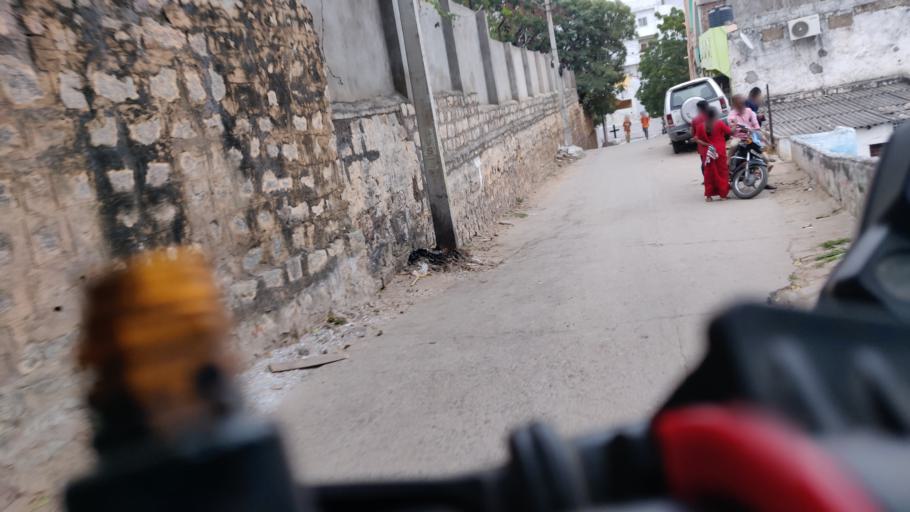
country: IN
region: Telangana
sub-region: Rangareddi
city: Kukatpalli
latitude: 17.4516
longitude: 78.4113
